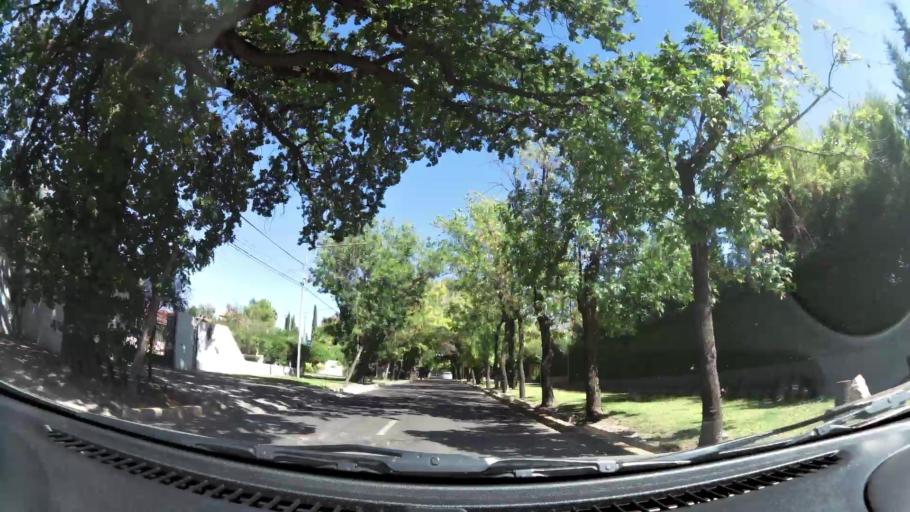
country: AR
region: Mendoza
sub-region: Departamento de Godoy Cruz
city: Godoy Cruz
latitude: -32.9614
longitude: -68.8574
